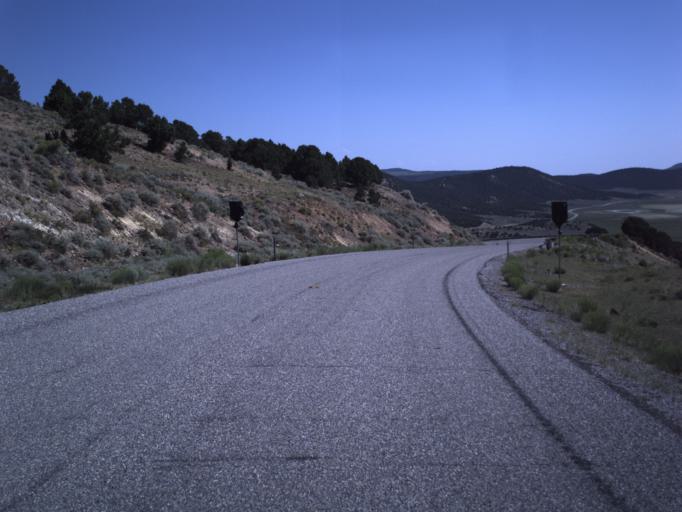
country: US
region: Utah
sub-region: Wayne County
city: Loa
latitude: 38.6069
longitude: -111.4623
